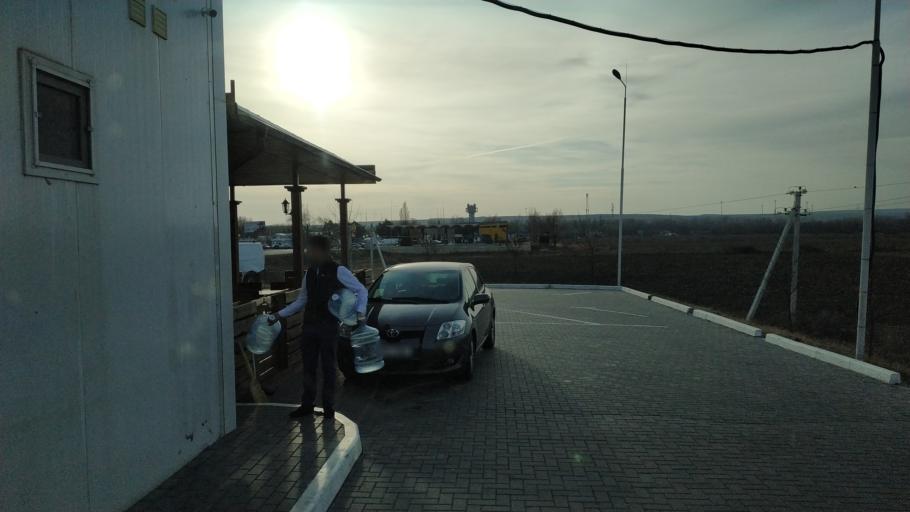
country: RO
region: Vaslui
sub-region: Comuna Dranceni
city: Rasesti
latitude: 46.7955
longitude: 28.1683
